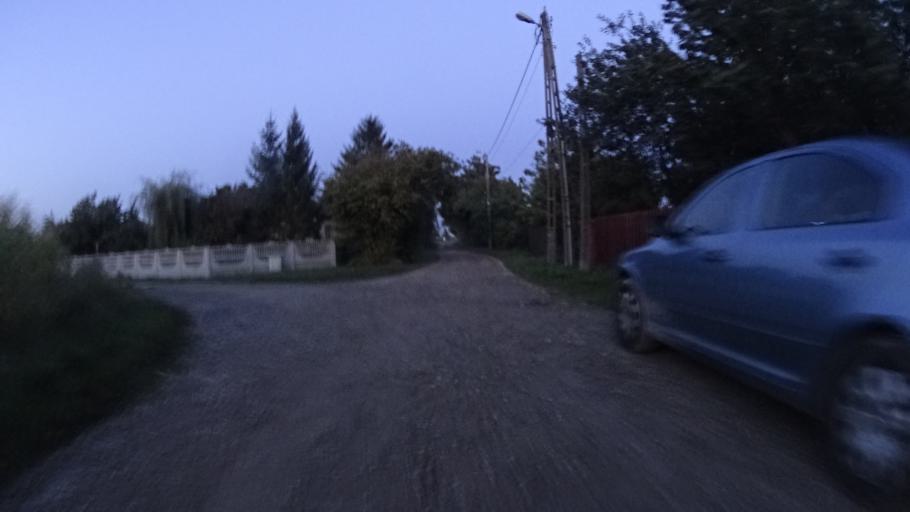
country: PL
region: Masovian Voivodeship
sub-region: Powiat warszawski zachodni
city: Ozarow Mazowiecki
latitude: 52.2226
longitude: 20.7855
